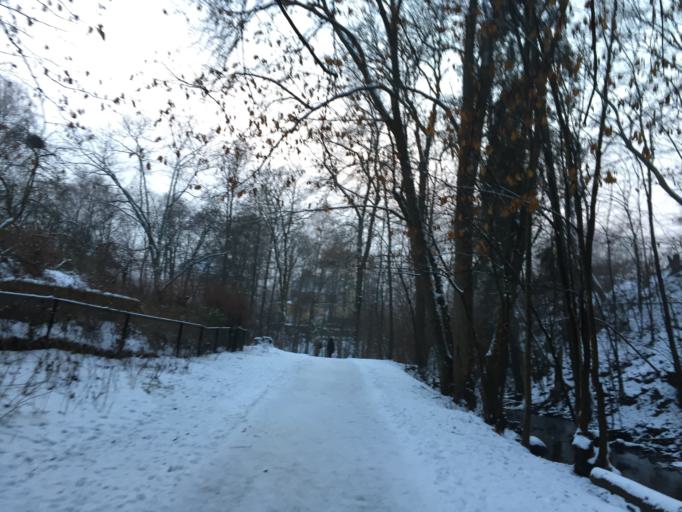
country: NO
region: Oslo
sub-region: Oslo
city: Sjolyststranda
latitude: 59.9225
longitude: 10.6953
